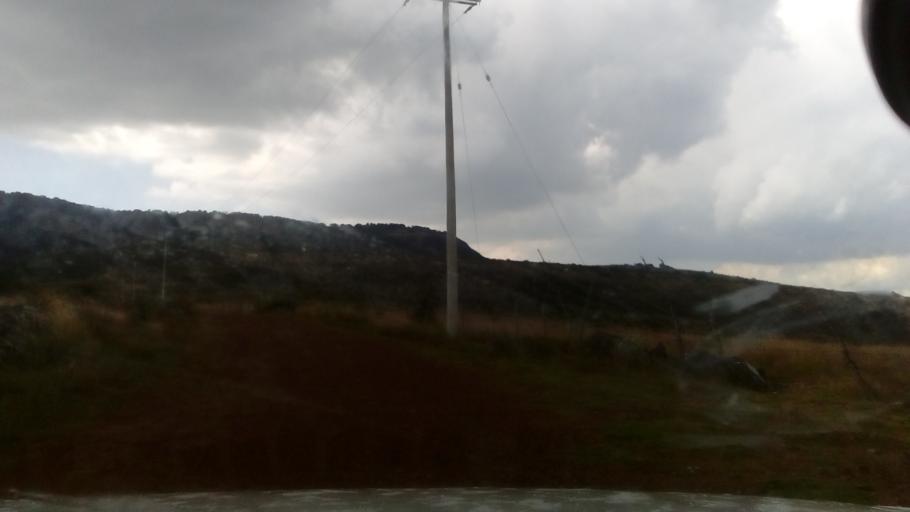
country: MX
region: Guanajuato
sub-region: Silao de la Victoria
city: San Francisco (Banos de Agua Caliente)
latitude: 21.1601
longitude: -101.4294
